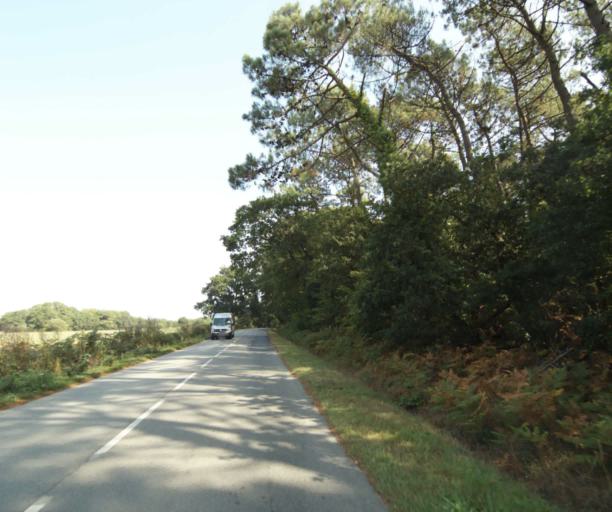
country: FR
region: Brittany
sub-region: Departement du Morbihan
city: Riantec
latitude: 47.7081
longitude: -3.2720
